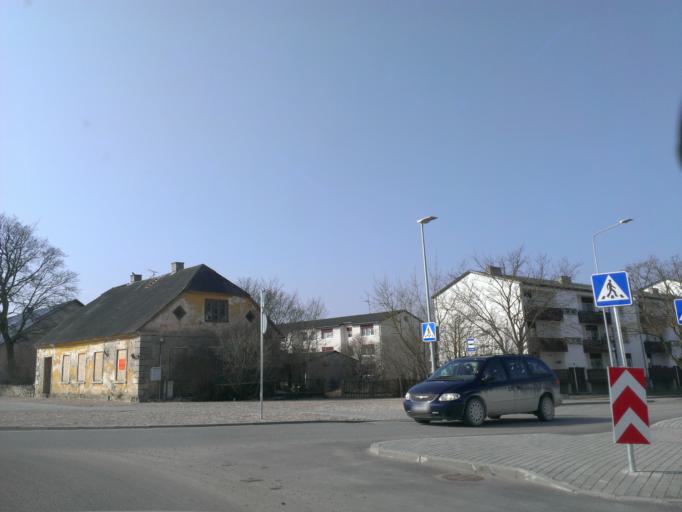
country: EE
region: Saare
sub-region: Kuressaare linn
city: Kuressaare
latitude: 58.2623
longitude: 22.4839
